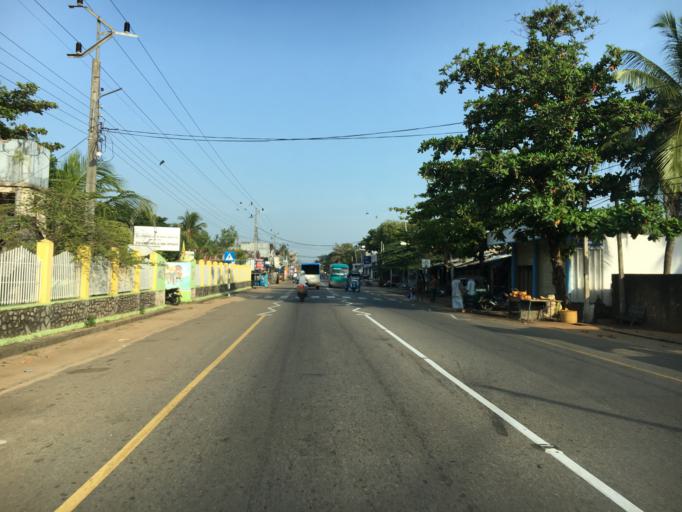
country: LK
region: Eastern Province
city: Eravur Town
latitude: 7.9109
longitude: 81.5294
